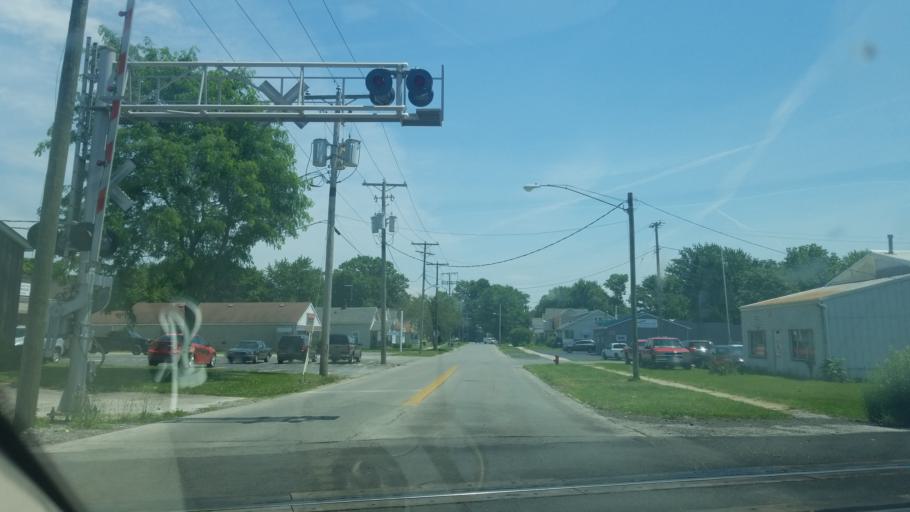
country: US
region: Ohio
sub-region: Hancock County
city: Findlay
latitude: 41.0467
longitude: -83.6447
